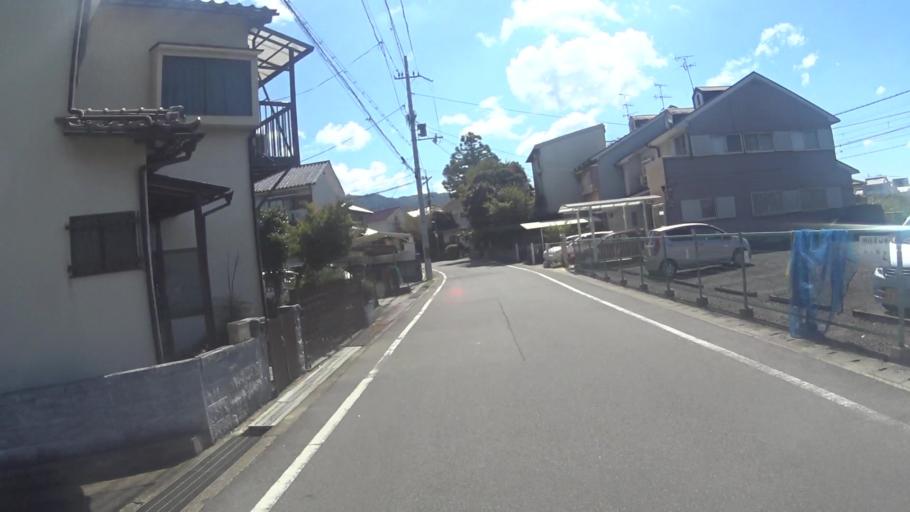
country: JP
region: Kyoto
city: Tanabe
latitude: 34.8271
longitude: 135.8017
